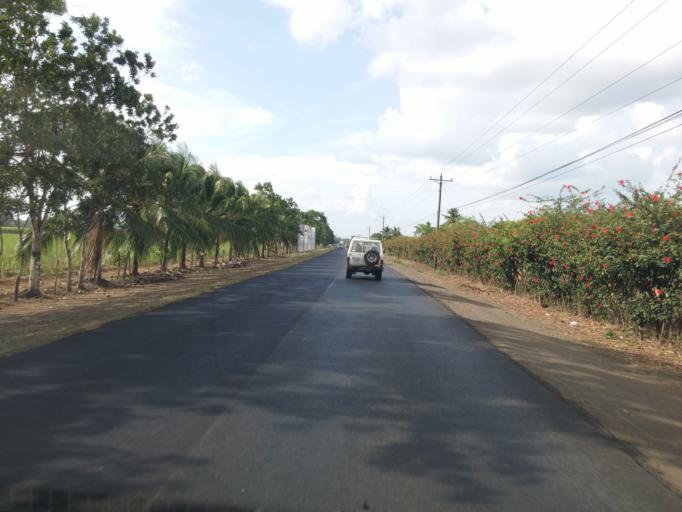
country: CR
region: Alajuela
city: Quesada
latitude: 10.4453
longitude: -84.4657
